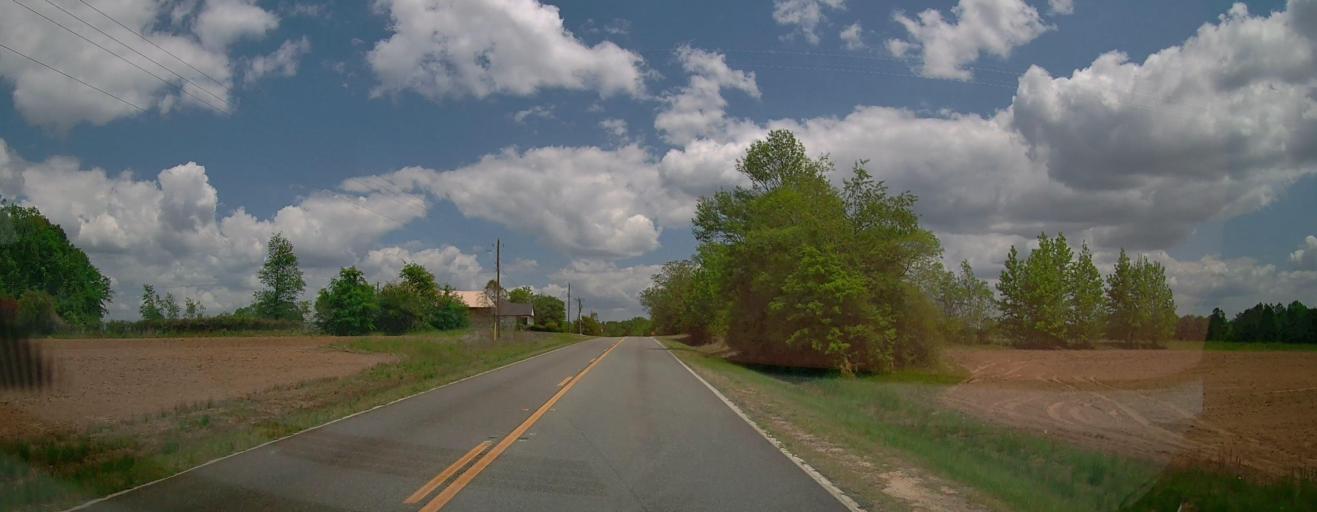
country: US
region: Georgia
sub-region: Laurens County
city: East Dublin
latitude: 32.5249
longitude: -82.7388
